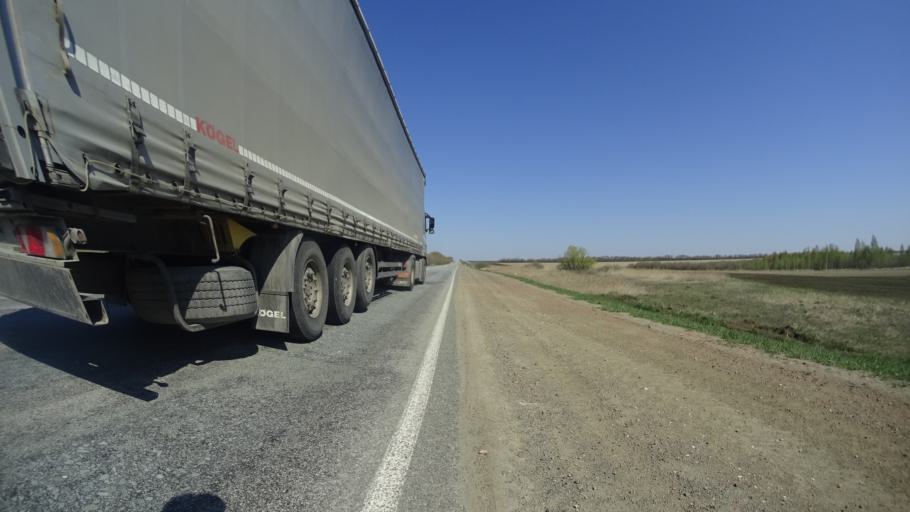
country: RU
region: Chelyabinsk
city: Troitsk
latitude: 54.2017
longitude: 61.4320
